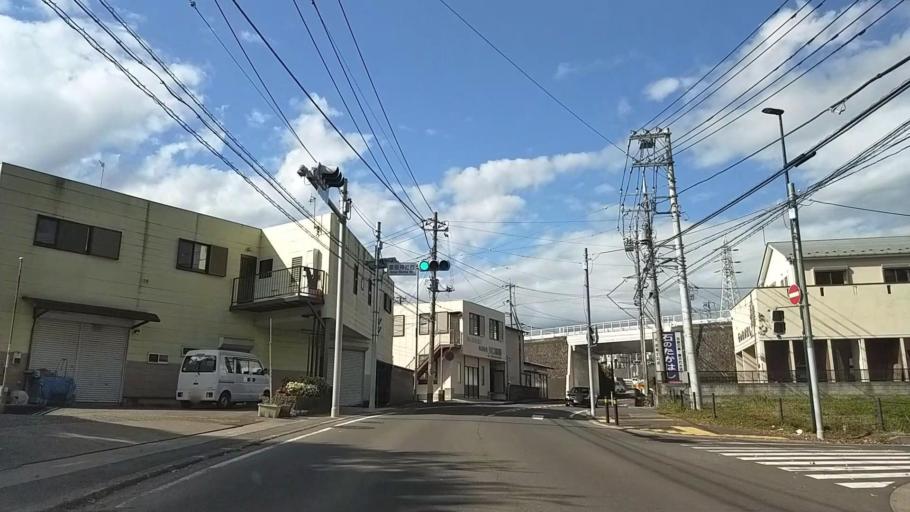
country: JP
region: Kanagawa
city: Hadano
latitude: 35.3797
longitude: 139.2195
